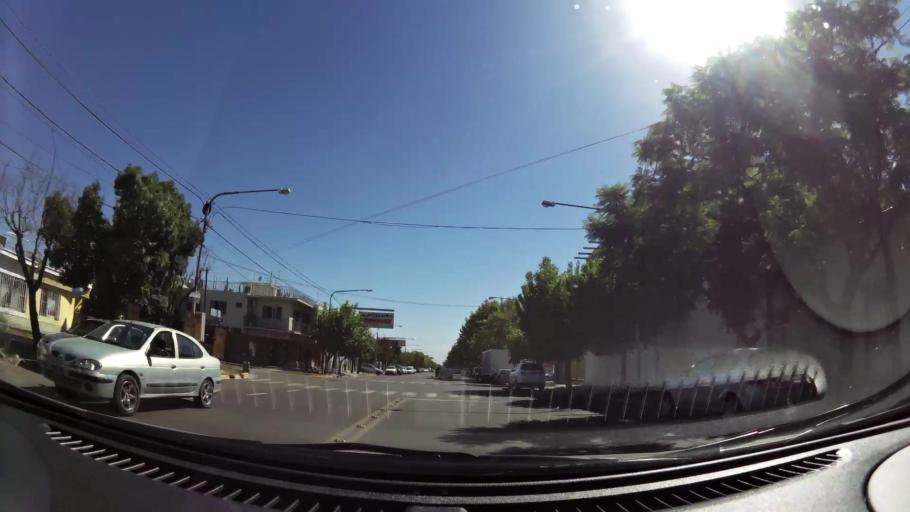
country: AR
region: Mendoza
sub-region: Departamento de Maipu
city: Maipu
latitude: -32.9554
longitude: -68.7888
